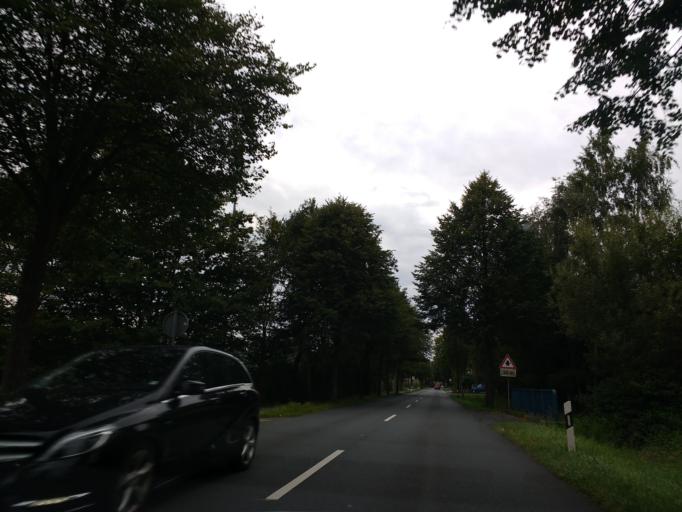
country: DE
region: North Rhine-Westphalia
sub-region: Regierungsbezirk Detmold
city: Delbruck
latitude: 51.7908
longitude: 8.5610
